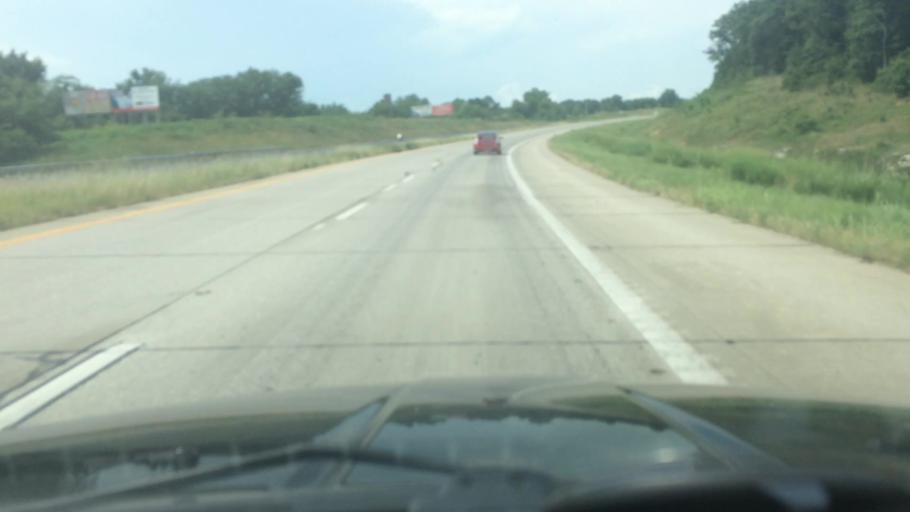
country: US
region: Missouri
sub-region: Saint Clair County
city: Osceola
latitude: 38.0851
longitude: -93.7067
